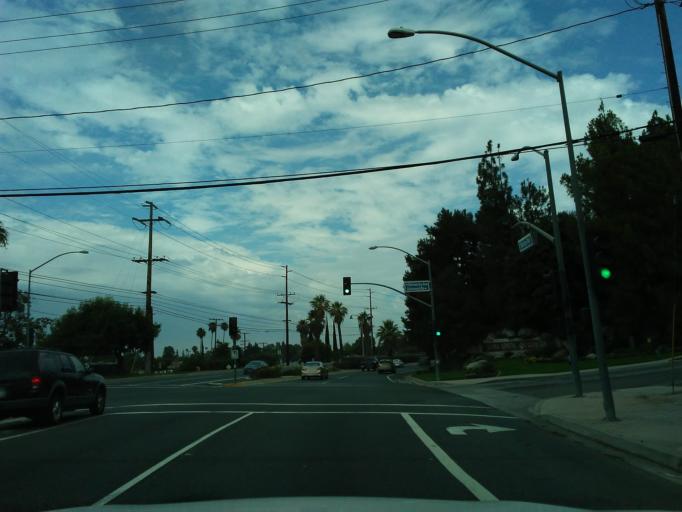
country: US
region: California
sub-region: San Bernardino County
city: Loma Linda
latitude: 34.0519
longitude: -117.2745
